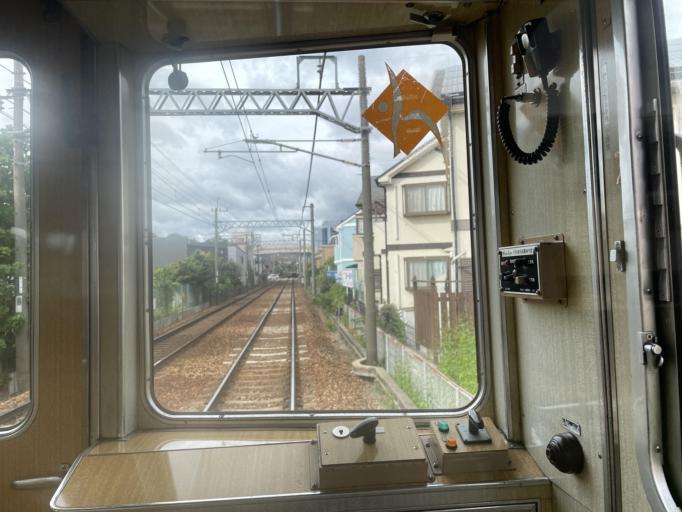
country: JP
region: Osaka
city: Ikeda
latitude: 34.8393
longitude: 135.4215
